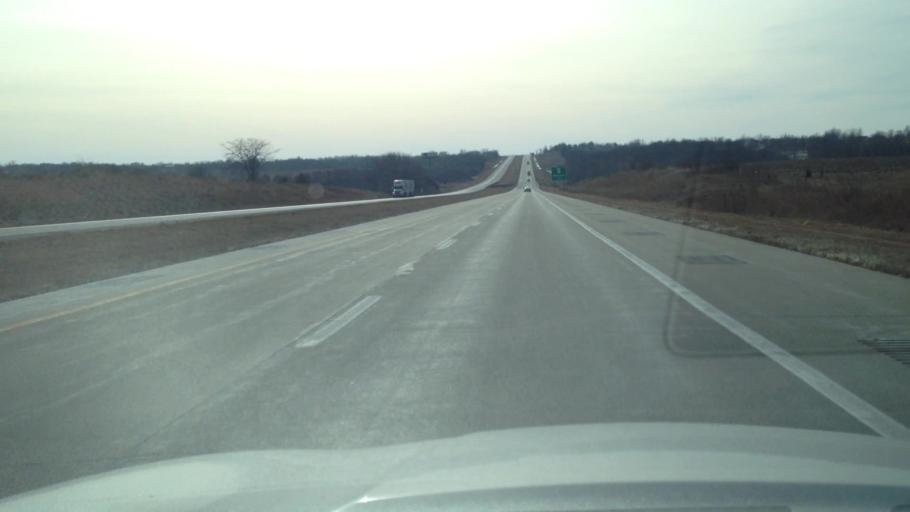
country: US
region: Missouri
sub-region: Harrison County
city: Bethany
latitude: 40.2999
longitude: -94.0122
